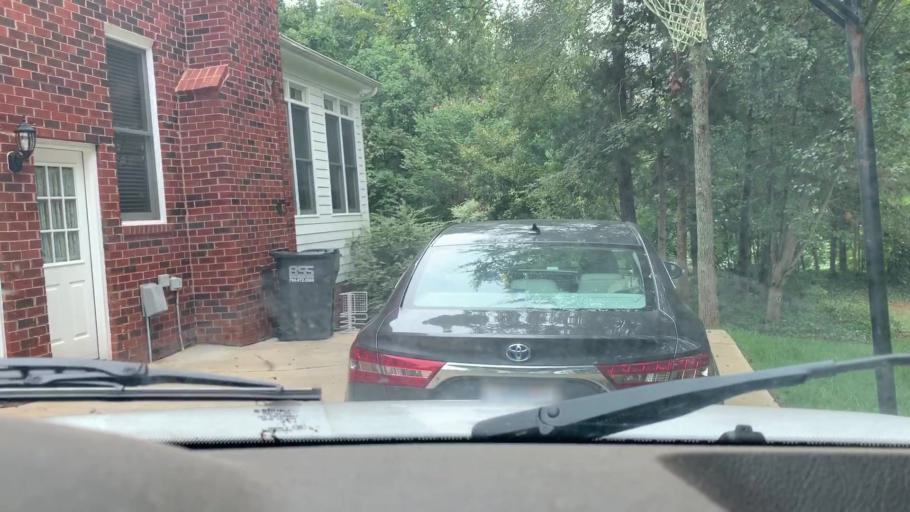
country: US
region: North Carolina
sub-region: Catawba County
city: Lake Norman of Catawba
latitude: 35.5517
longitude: -80.9105
